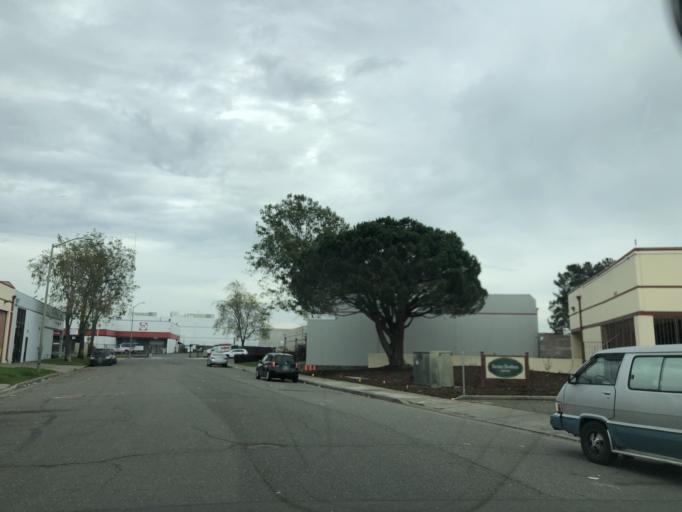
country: US
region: California
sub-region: Alameda County
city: San Leandro
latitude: 37.7279
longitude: -122.1959
